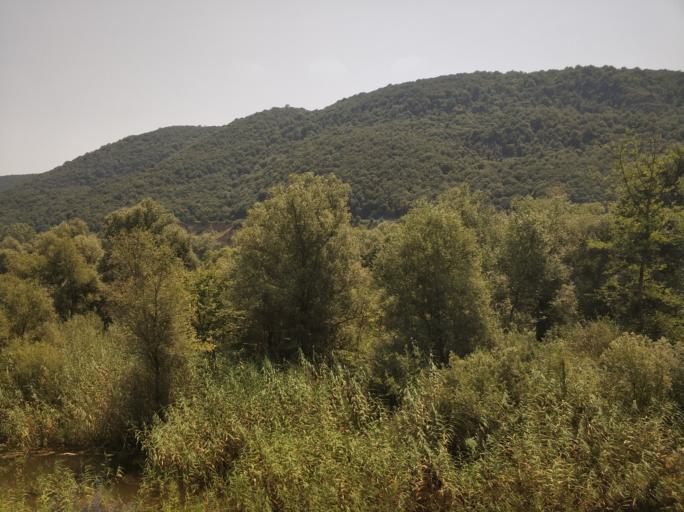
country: IR
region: Gilan
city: Pa'in-e Bazar-e Rudbar
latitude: 36.9832
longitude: 49.5575
